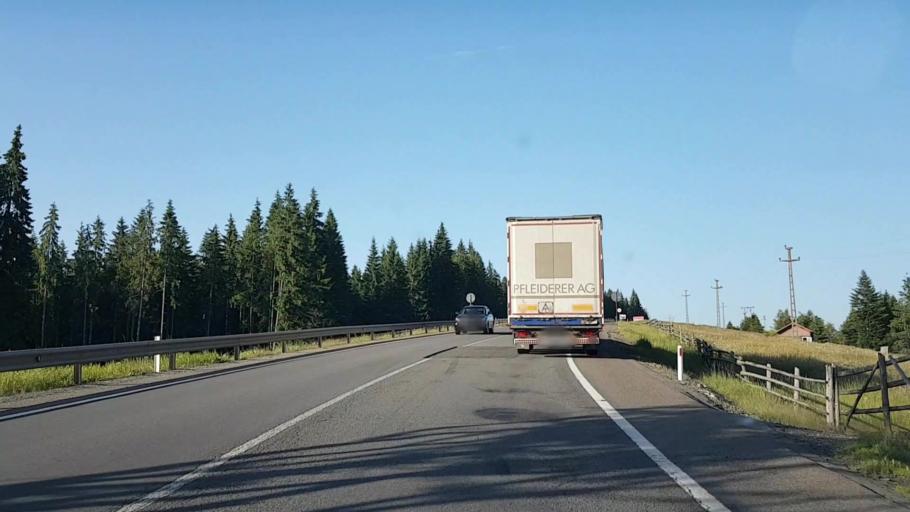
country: RO
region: Bistrita-Nasaud
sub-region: Comuna Lunca Ilvei
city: Lunca Ilvei
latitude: 47.2786
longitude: 25.0294
